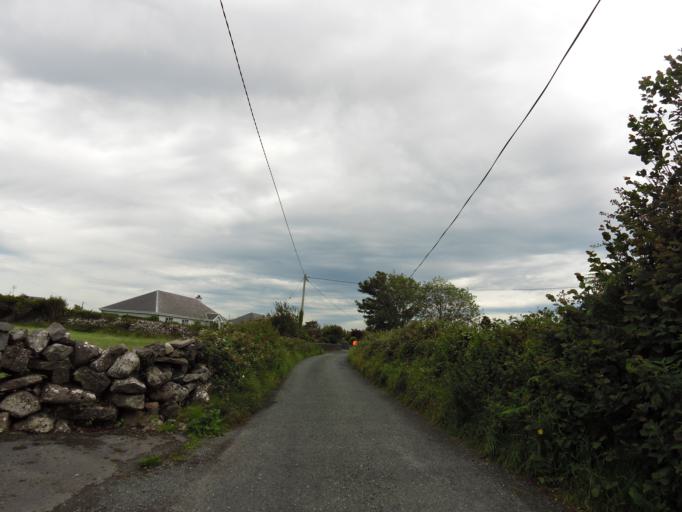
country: IE
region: Connaught
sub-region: County Galway
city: Gaillimh
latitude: 53.3159
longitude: -9.0444
